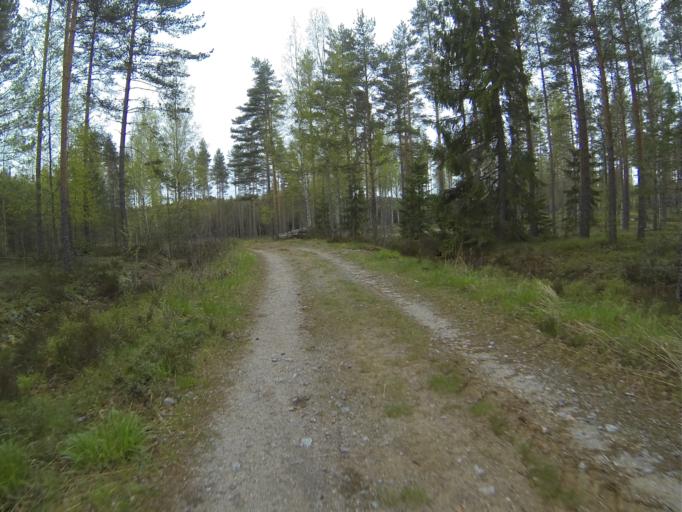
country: FI
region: Varsinais-Suomi
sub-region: Salo
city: Salo
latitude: 60.3894
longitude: 23.1993
